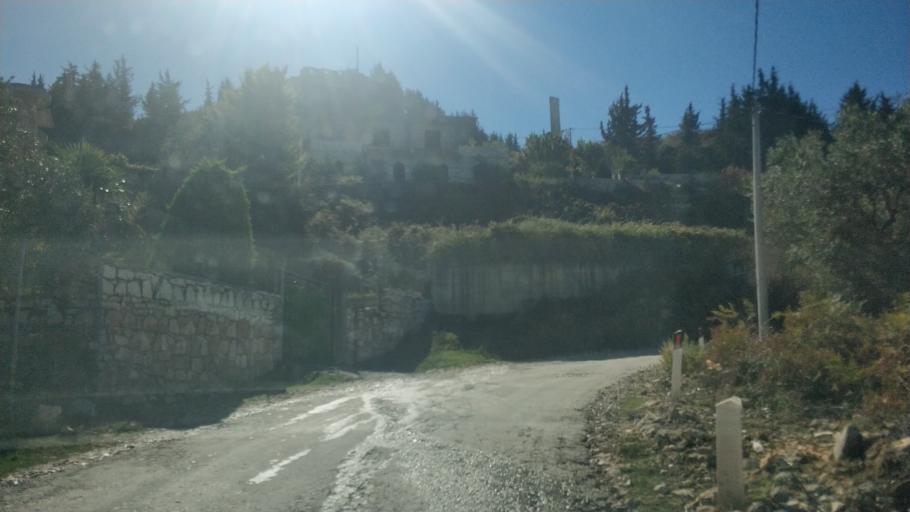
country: AL
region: Vlore
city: Vlore
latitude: 40.4461
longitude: 19.5191
